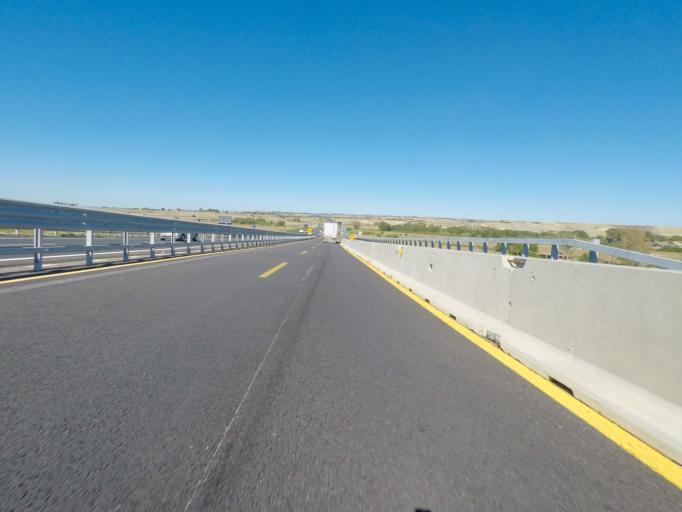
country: IT
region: Latium
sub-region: Citta metropolitana di Roma Capitale
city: Aurelia
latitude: 42.1887
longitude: 11.7864
